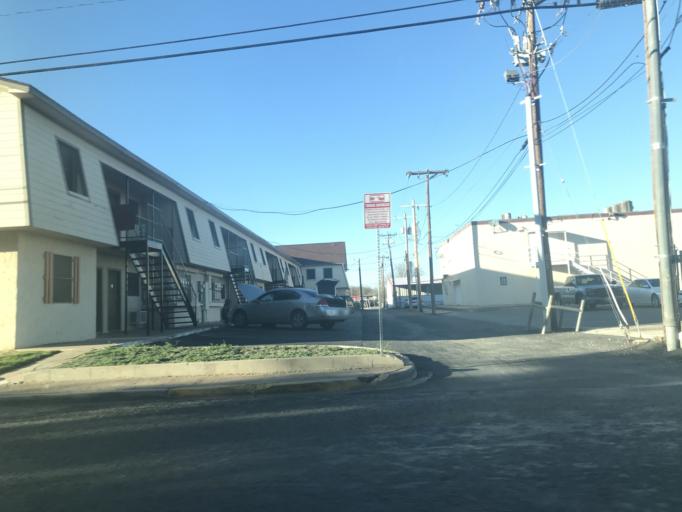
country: US
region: Texas
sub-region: Tom Green County
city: San Angelo
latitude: 31.4420
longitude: -100.4592
